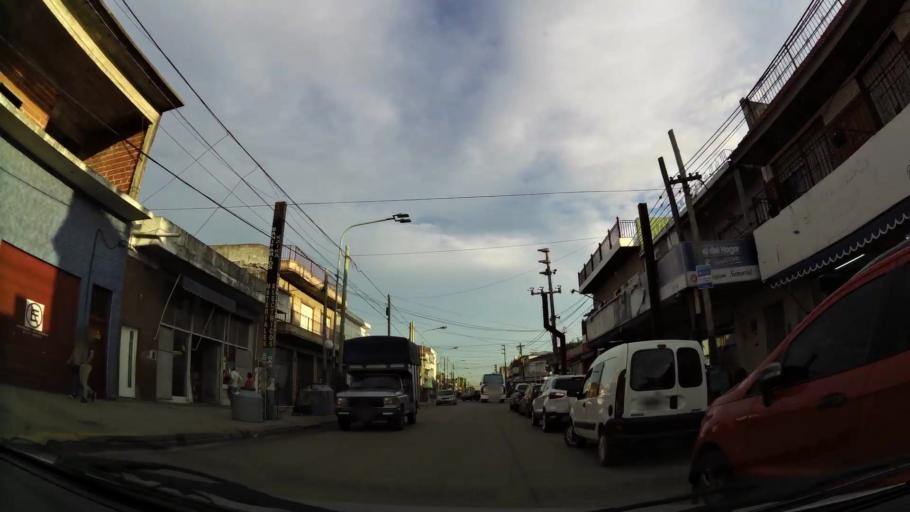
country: AR
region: Buenos Aires
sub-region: Partido de Almirante Brown
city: Adrogue
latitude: -34.7733
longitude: -58.3525
